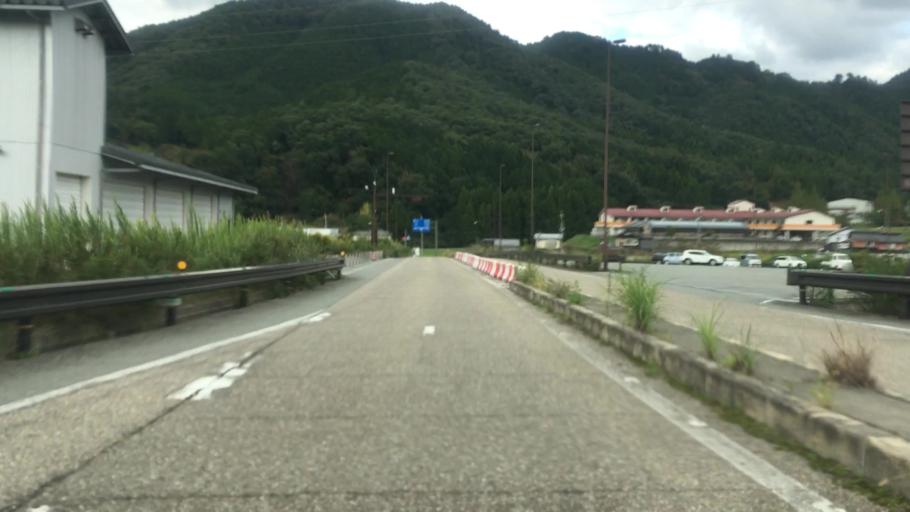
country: JP
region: Kyoto
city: Fukuchiyama
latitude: 35.3040
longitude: 134.9080
